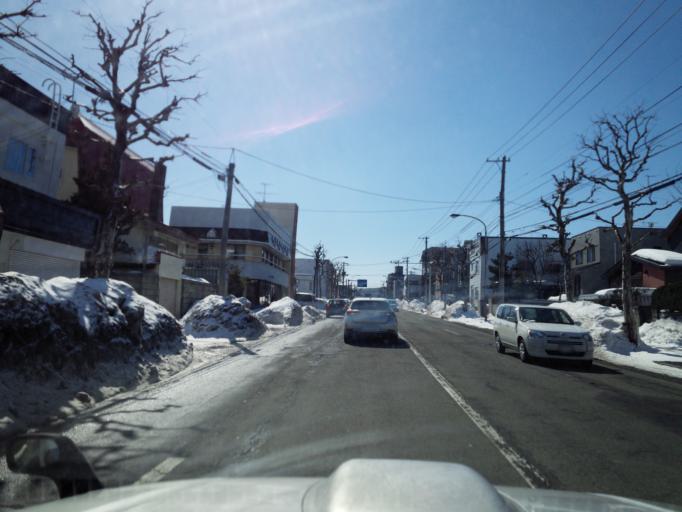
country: JP
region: Hokkaido
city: Sapporo
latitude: 43.0044
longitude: 141.4306
